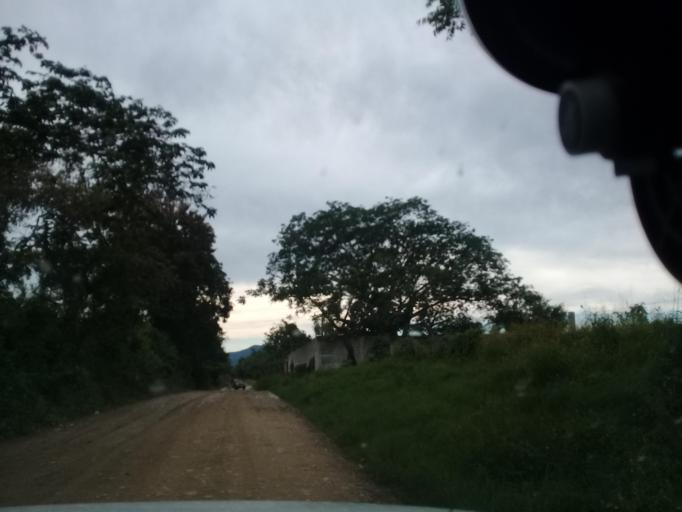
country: MX
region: Hidalgo
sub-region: Huejutla de Reyes
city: Parque de Poblamiento Solidaridad
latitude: 21.1562
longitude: -98.3752
